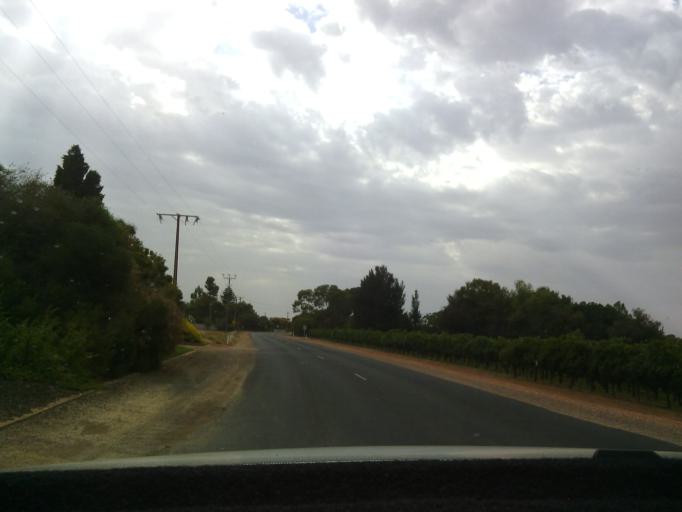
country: AU
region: South Australia
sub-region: Berri and Barmera
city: Berri
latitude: -34.2654
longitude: 140.5862
